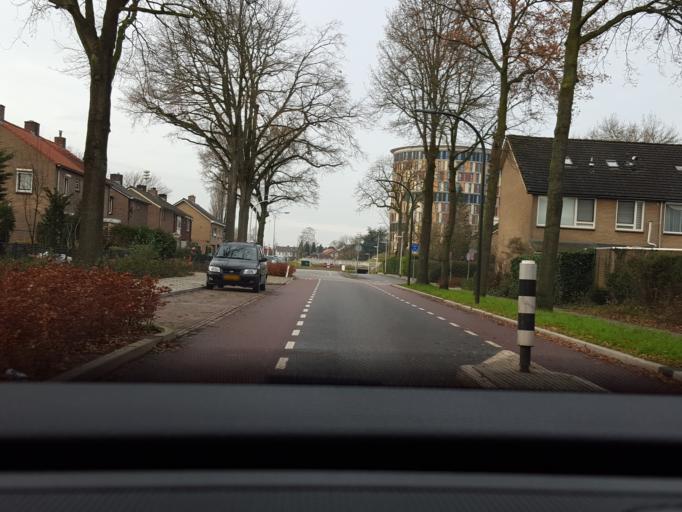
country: NL
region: Gelderland
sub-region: Gemeente Lochem
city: Eefde
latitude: 52.1505
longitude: 6.2192
